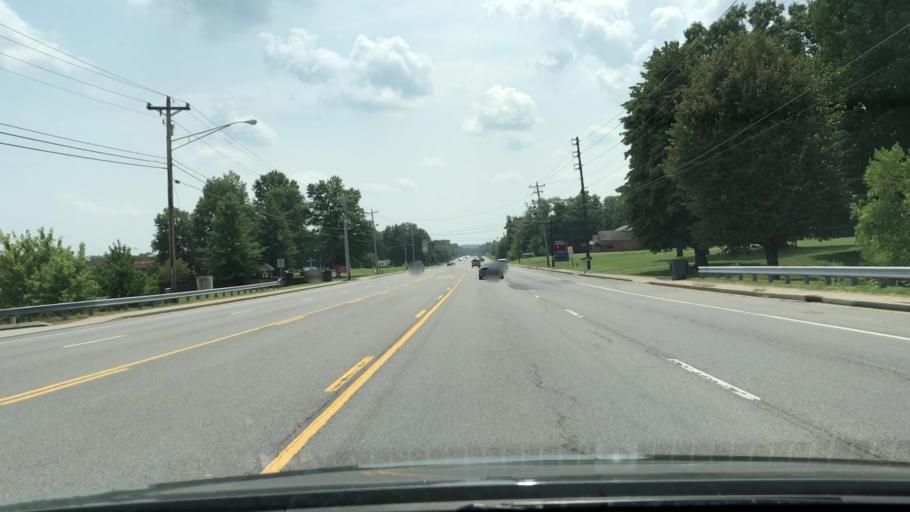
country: US
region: Tennessee
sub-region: Sumner County
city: Portland
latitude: 36.5585
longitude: -86.5091
